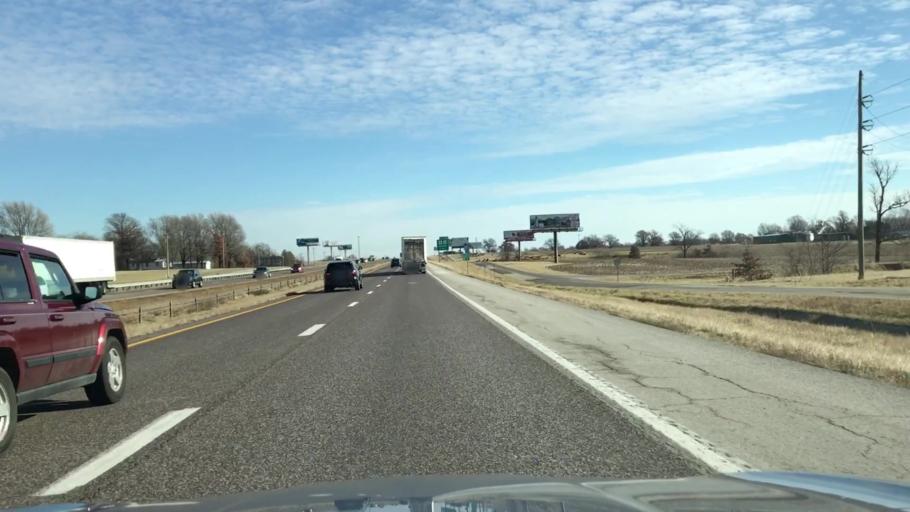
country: US
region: Missouri
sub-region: Callaway County
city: Fulton
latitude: 38.9520
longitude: -92.0337
